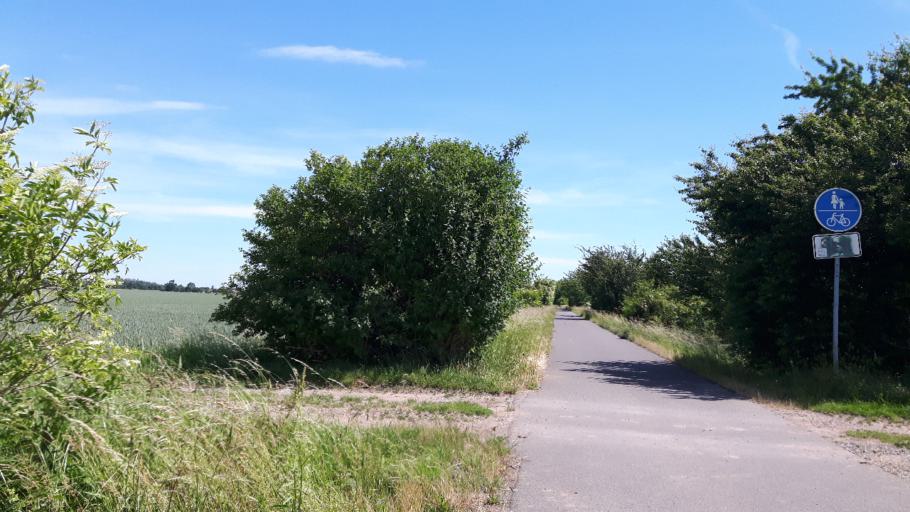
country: DE
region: Saxony
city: Kitzen
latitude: 51.2545
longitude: 12.1947
